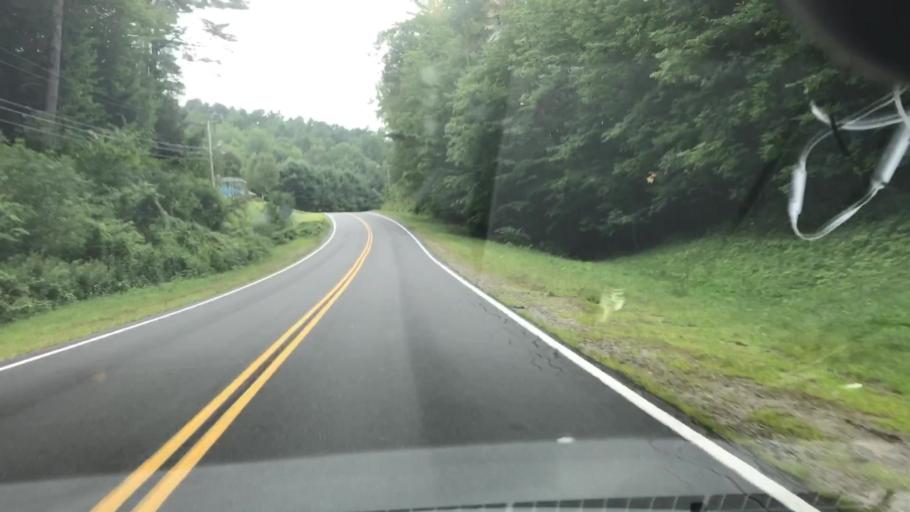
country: US
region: New Hampshire
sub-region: Grafton County
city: Woodsville
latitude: 44.2414
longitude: -72.0422
